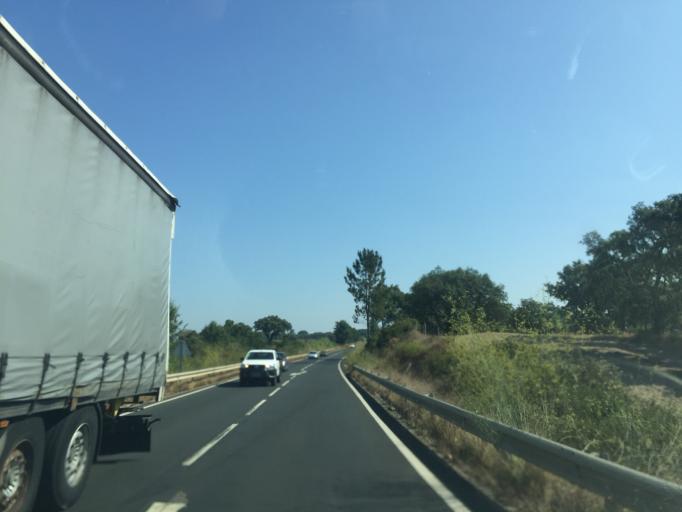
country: PT
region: Santarem
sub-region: Alpiarca
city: Alpiarca
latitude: 39.2772
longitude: -8.5445
